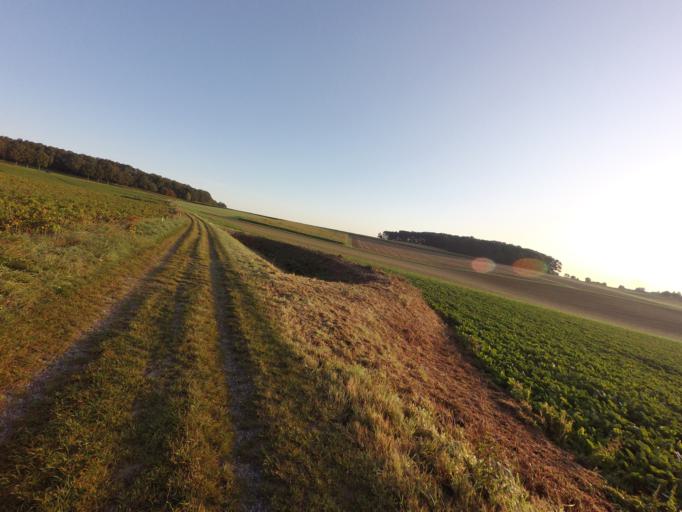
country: NL
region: Limburg
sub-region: Gemeente Voerendaal
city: Ubachsberg
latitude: 50.8426
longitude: 5.9561
